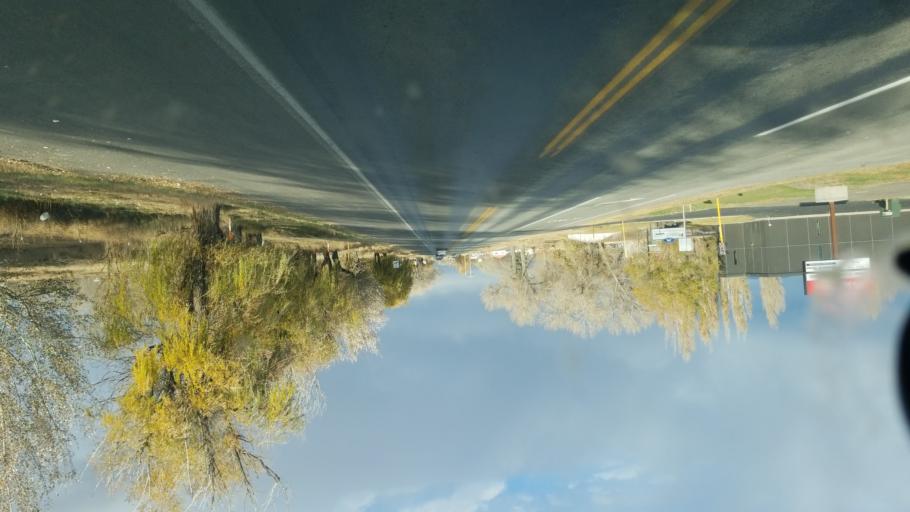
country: US
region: Colorado
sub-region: Alamosa County
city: Alamosa East
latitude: 37.4731
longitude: -105.8532
